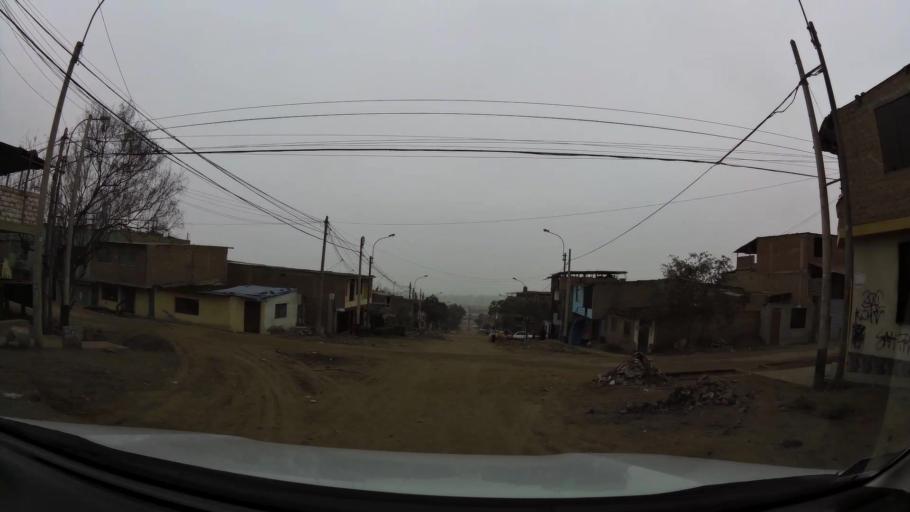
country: PE
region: Lima
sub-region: Lima
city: Surco
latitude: -12.1889
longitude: -76.9317
